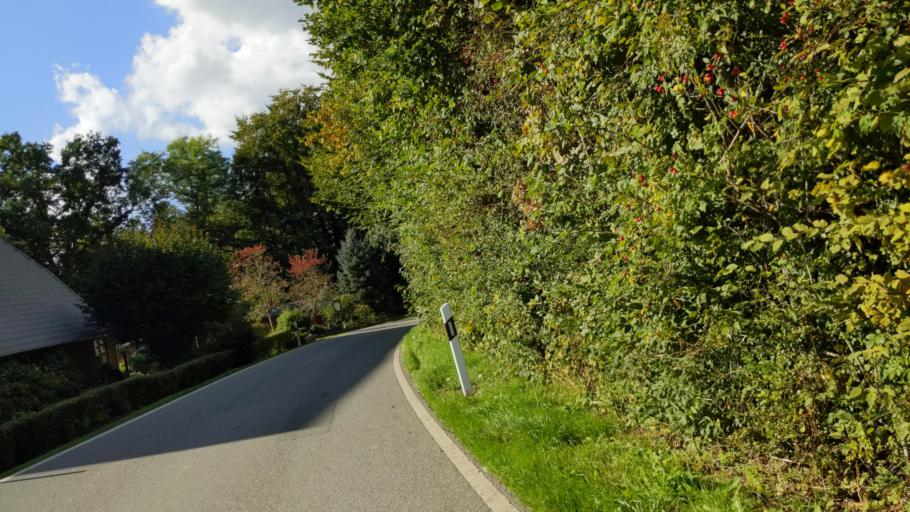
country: DE
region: Schleswig-Holstein
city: Ahrensbok
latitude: 53.9940
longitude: 10.5904
